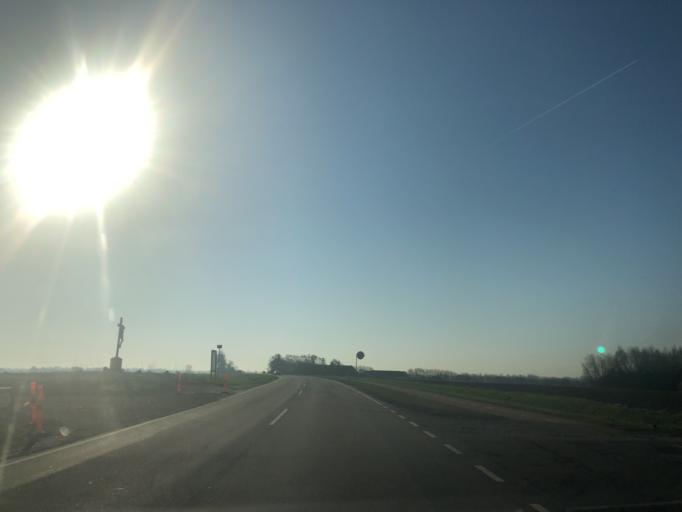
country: DK
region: Zealand
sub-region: Faxe Kommune
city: Haslev
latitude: 55.3679
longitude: 11.8674
